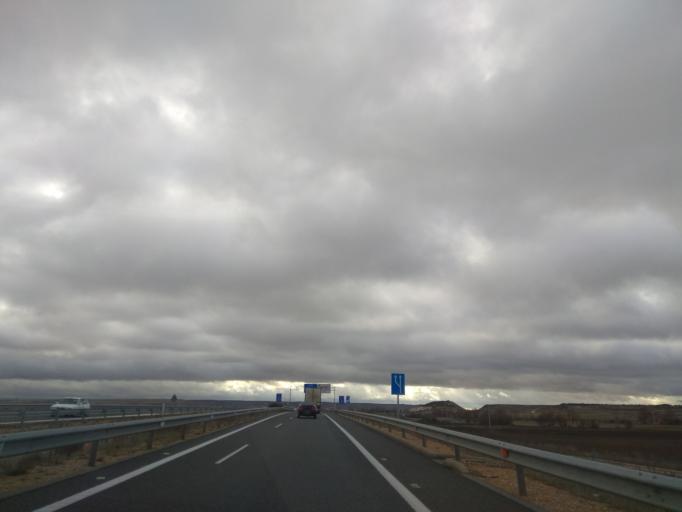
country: ES
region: Castille and Leon
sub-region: Provincia de Burgos
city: Quintanaortuno
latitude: 42.4704
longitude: -3.6894
